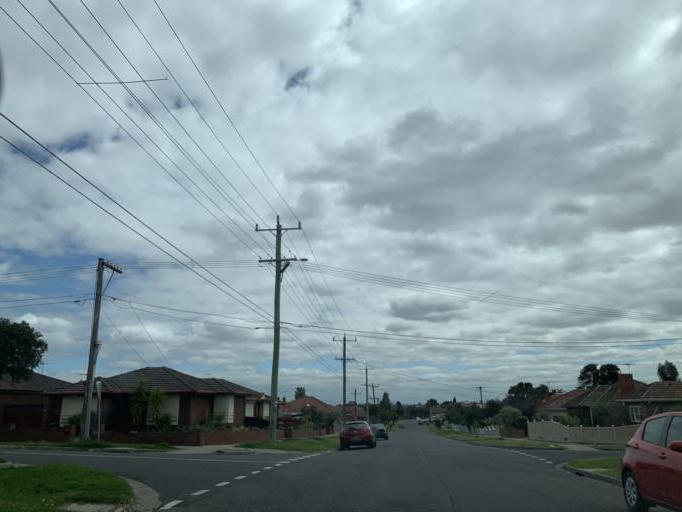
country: AU
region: Victoria
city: Thornbury
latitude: -37.7412
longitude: 144.9886
